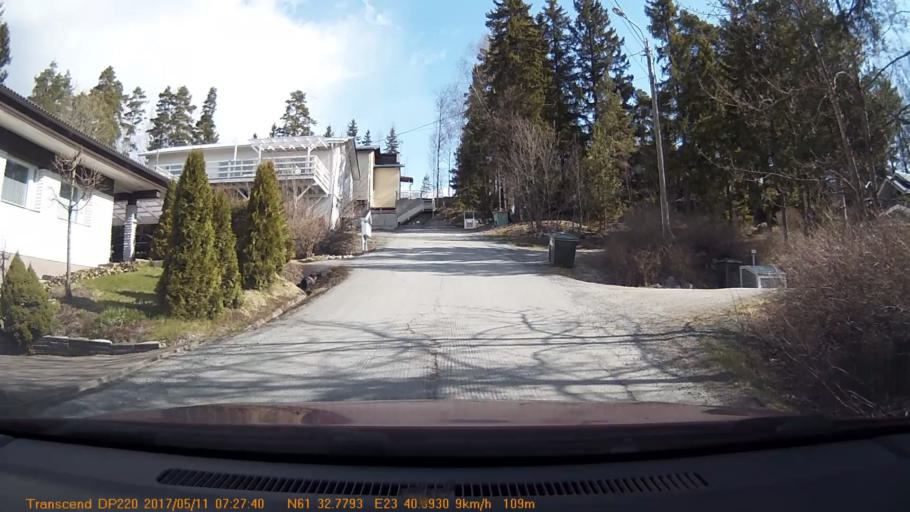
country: FI
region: Pirkanmaa
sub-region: Tampere
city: Yloejaervi
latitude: 61.5464
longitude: 23.6817
